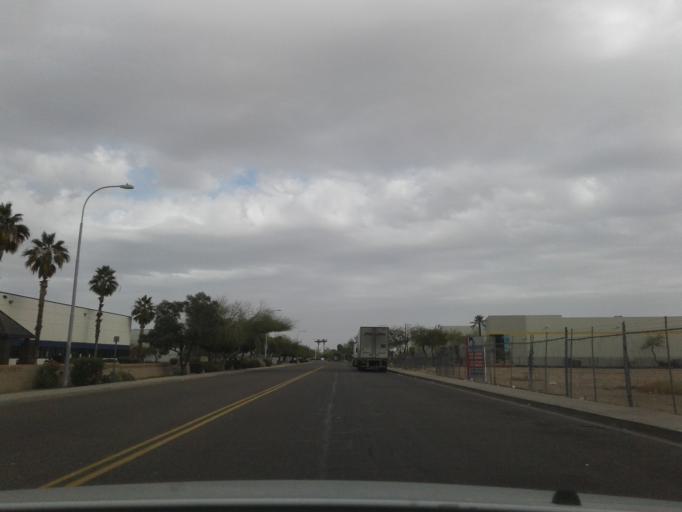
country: US
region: Arizona
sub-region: Maricopa County
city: Glendale
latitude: 33.4611
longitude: -112.1629
